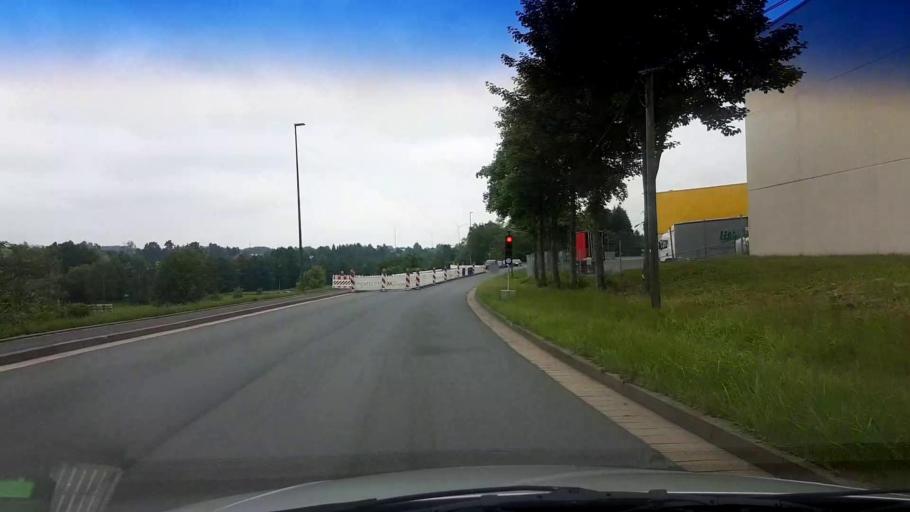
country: DE
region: Bavaria
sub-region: Upper Franconia
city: Marktredwitz
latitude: 50.0171
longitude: 12.0979
